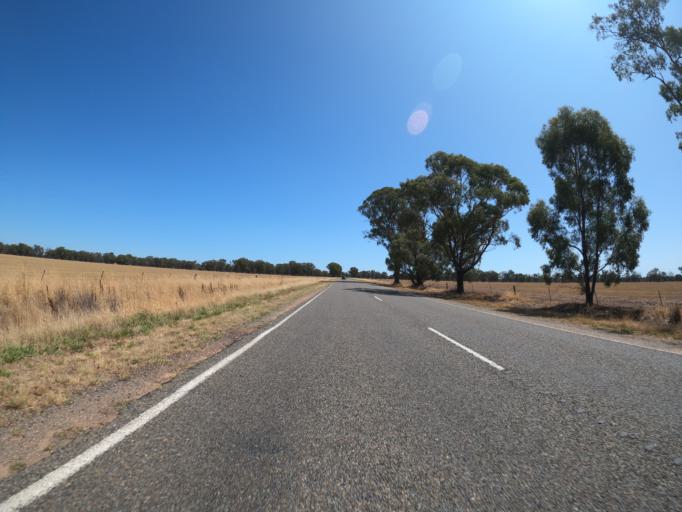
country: AU
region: New South Wales
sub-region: Corowa Shire
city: Corowa
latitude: -36.0786
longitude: 146.3424
